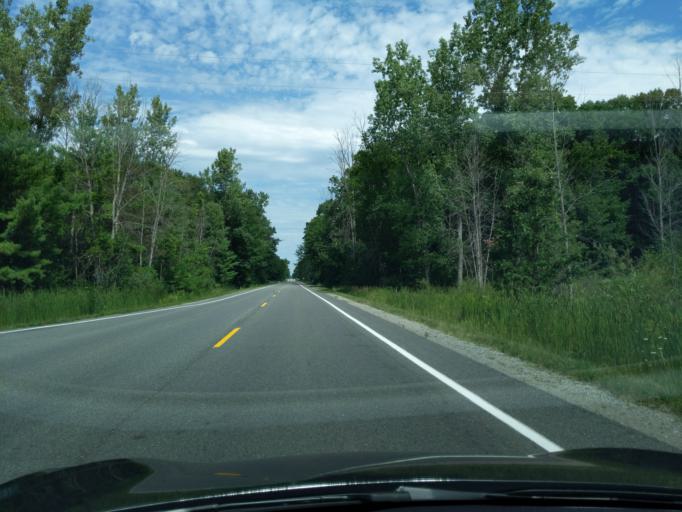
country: US
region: Michigan
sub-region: Midland County
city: Midland
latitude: 43.5894
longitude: -84.3693
